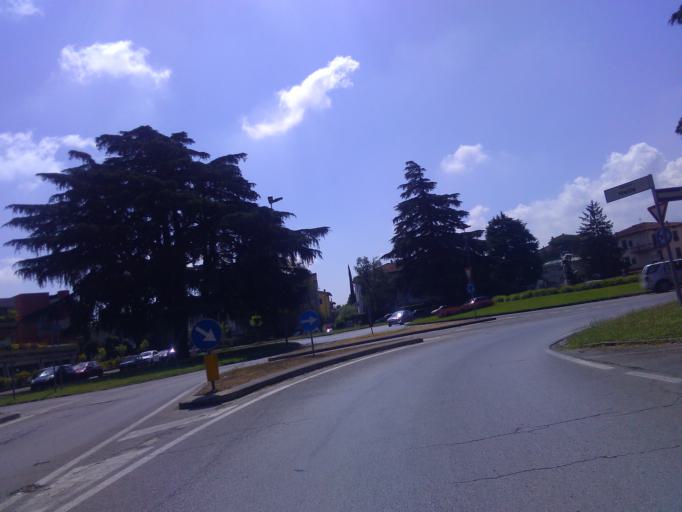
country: IT
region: Tuscany
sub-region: Provincia di Lucca
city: Lucca
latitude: 43.8417
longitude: 10.4915
